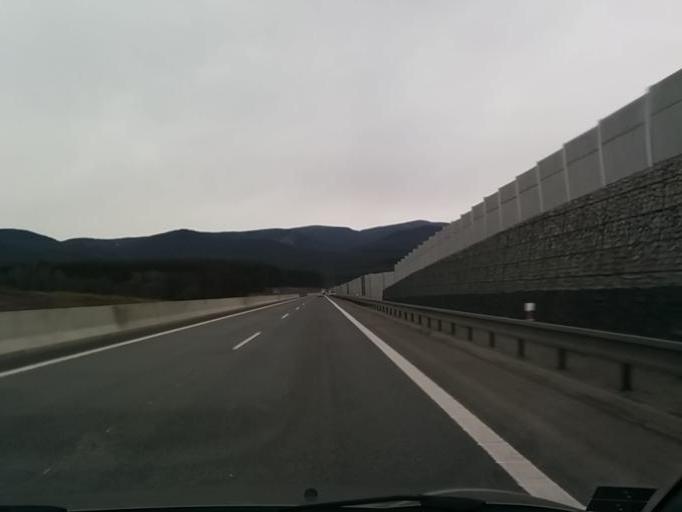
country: SK
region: Nitriansky
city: Tlmace
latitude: 48.3619
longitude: 18.4990
